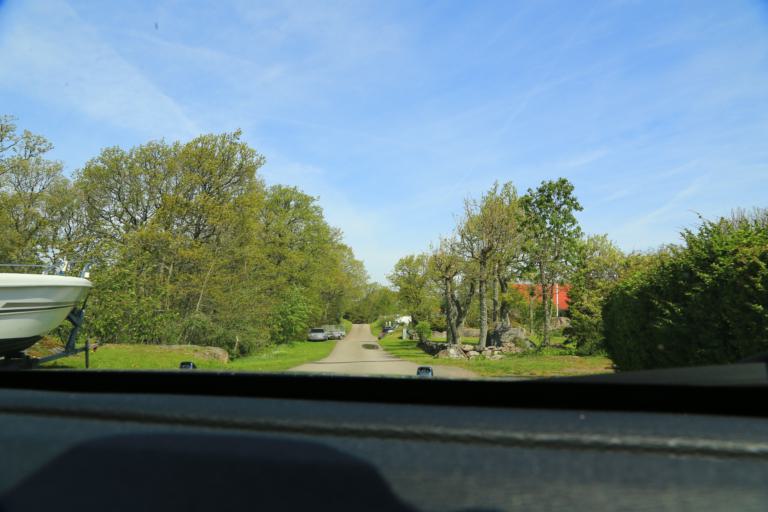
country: SE
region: Halland
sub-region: Varbergs Kommun
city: Varberg
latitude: 57.1348
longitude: 12.2235
